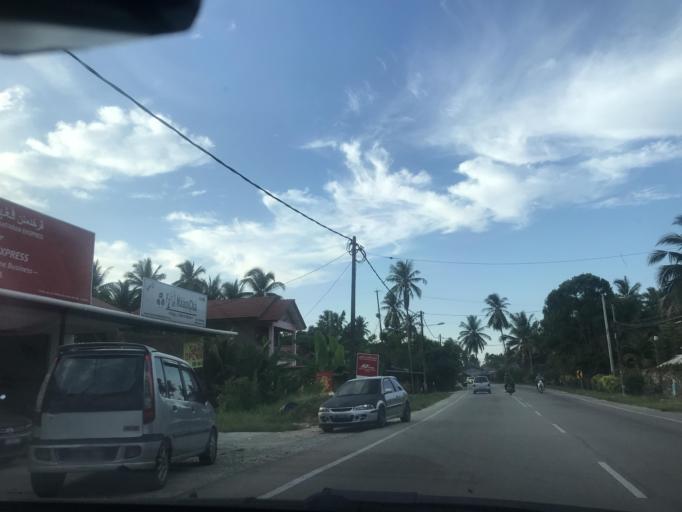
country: MY
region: Kelantan
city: Peringat
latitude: 6.1220
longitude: 102.3570
